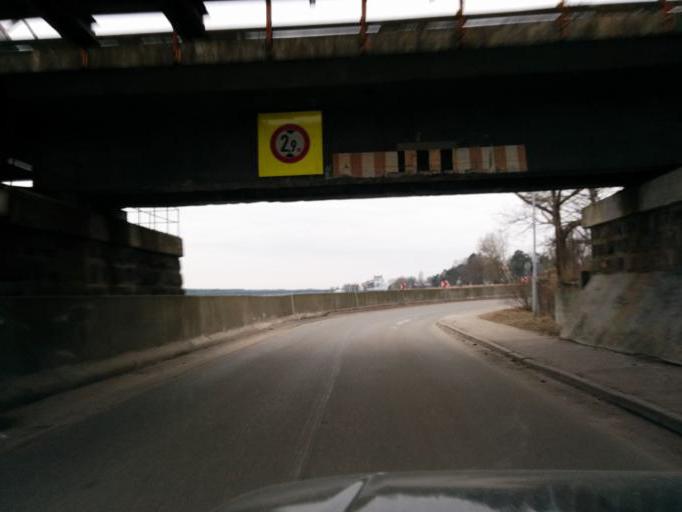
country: LV
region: Babite
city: Pinki
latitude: 56.9799
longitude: 23.8744
